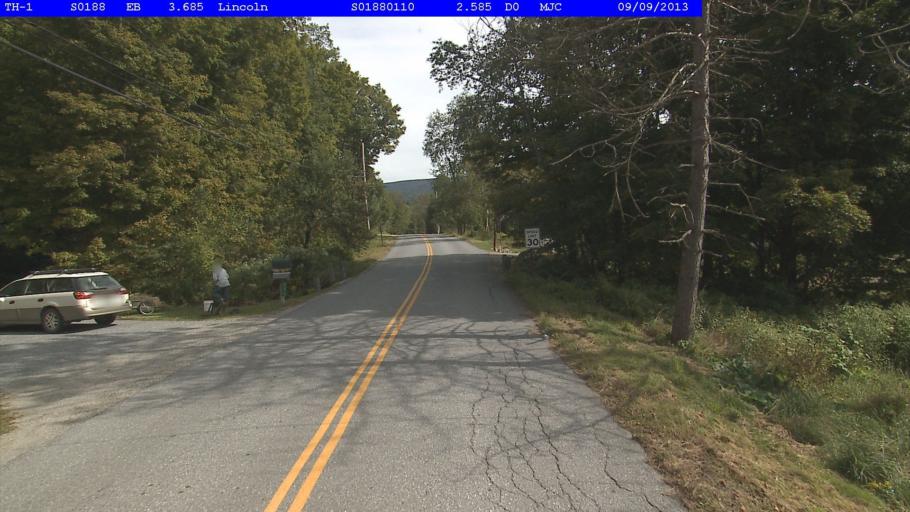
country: US
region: Vermont
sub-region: Addison County
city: Bristol
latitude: 44.1024
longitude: -72.9930
